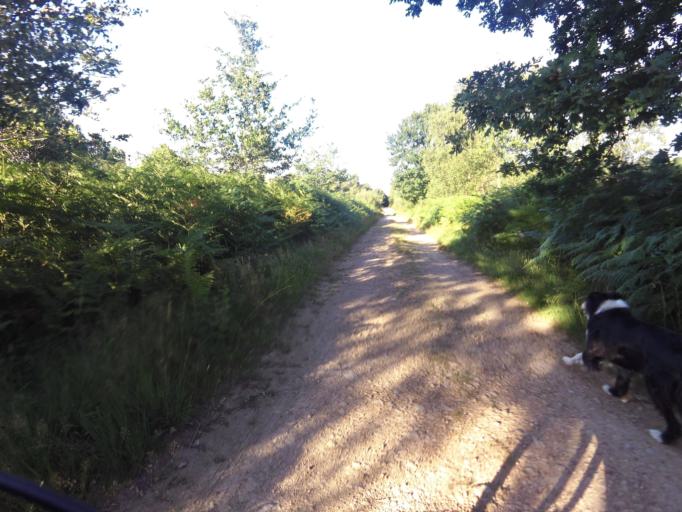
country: FR
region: Brittany
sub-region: Departement du Morbihan
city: Molac
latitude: 47.7561
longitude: -2.4297
